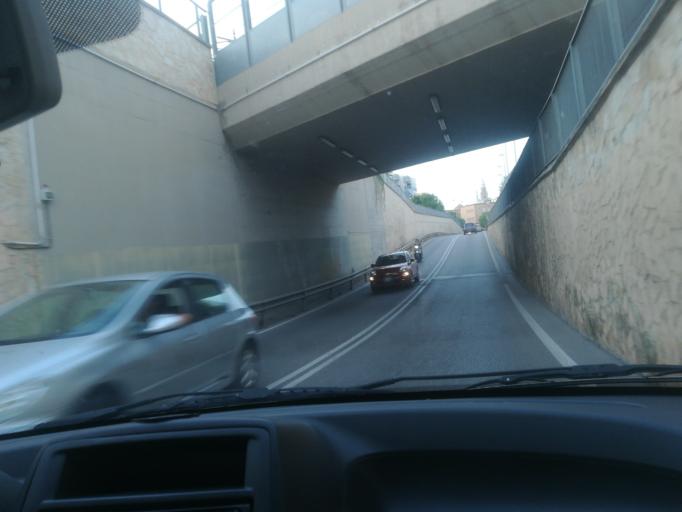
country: IT
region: Apulia
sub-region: Provincia di Bari
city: Monopoli
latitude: 40.9458
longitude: 17.3020
